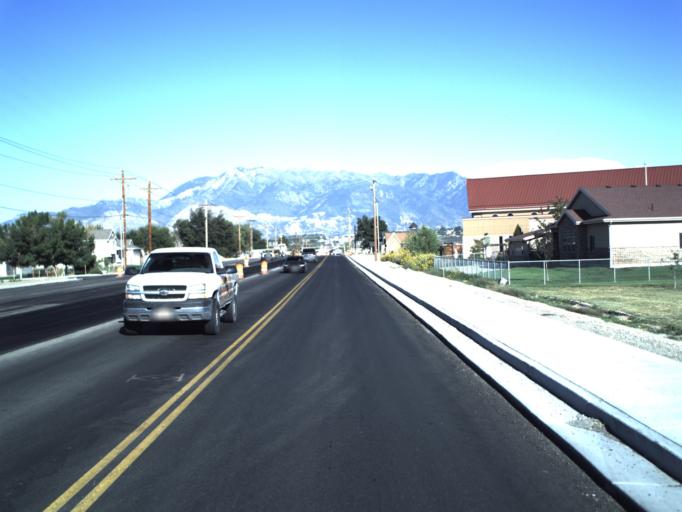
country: US
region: Utah
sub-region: Weber County
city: West Haven
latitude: 41.1907
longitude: -112.0736
